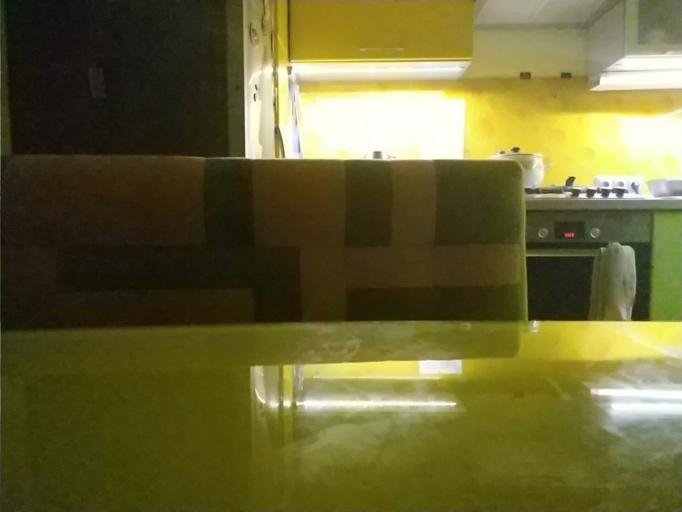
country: RU
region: Republic of Karelia
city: Pyaozerskiy
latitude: 65.9337
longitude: 30.4119
